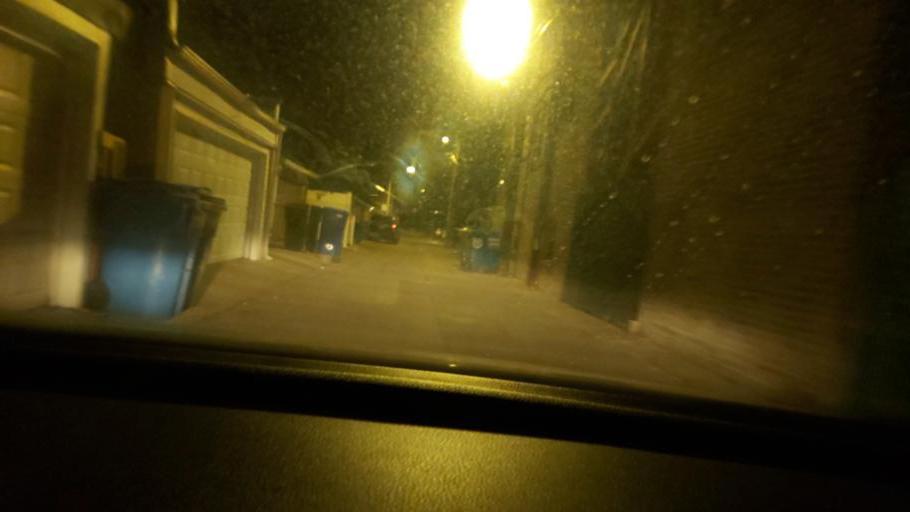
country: US
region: Illinois
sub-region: Cook County
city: Lincolnwood
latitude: 41.9854
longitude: -87.7132
